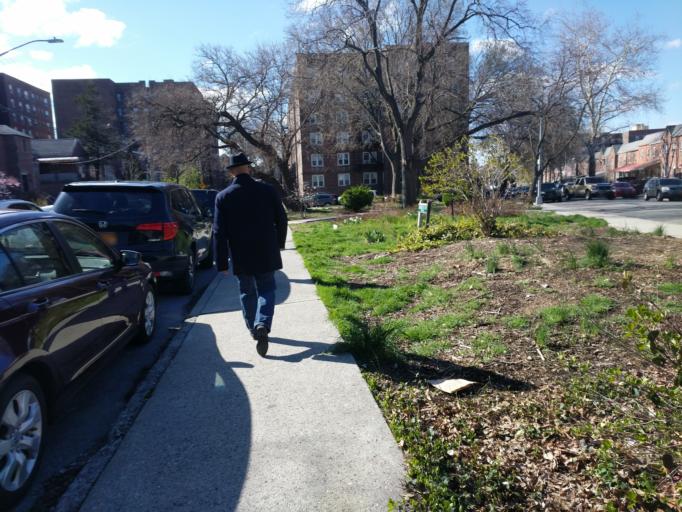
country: US
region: New York
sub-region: Bronx
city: The Bronx
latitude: 40.8562
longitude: -73.8609
